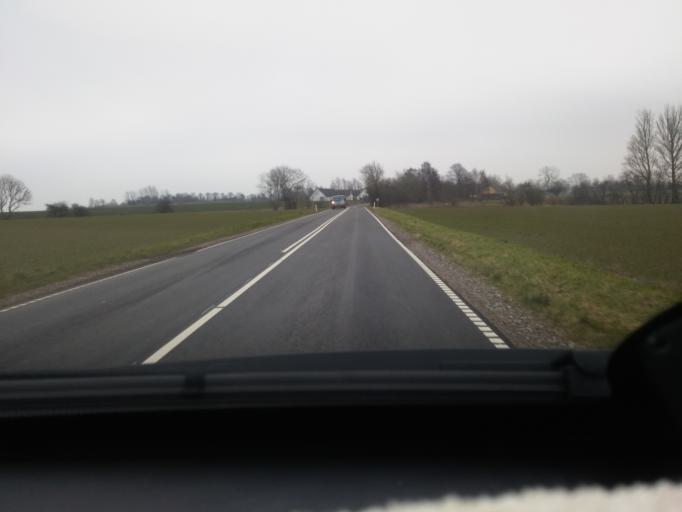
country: DK
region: South Denmark
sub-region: Kerteminde Kommune
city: Kerteminde
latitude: 55.4050
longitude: 10.7254
